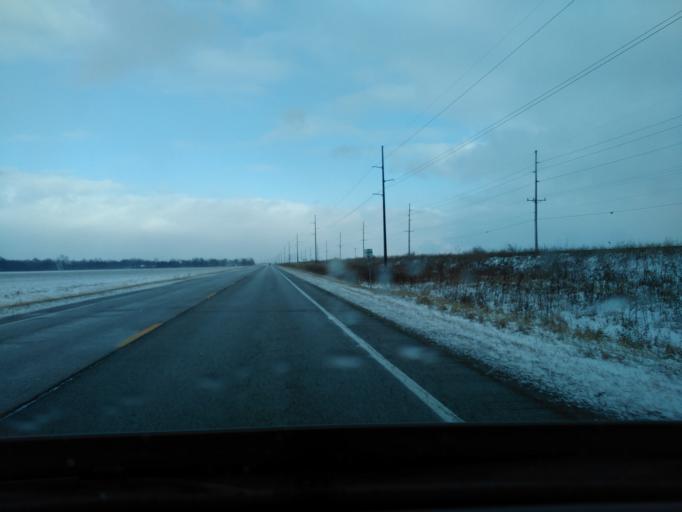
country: US
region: Illinois
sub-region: Madison County
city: Saint Jacob
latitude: 38.7224
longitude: -89.7584
